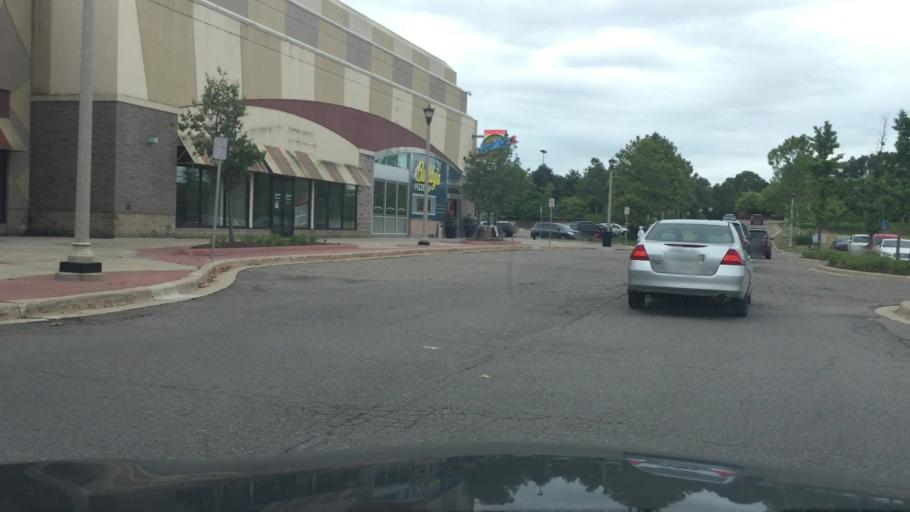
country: US
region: Michigan
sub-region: Oakland County
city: Novi
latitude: 42.4943
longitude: -83.4849
